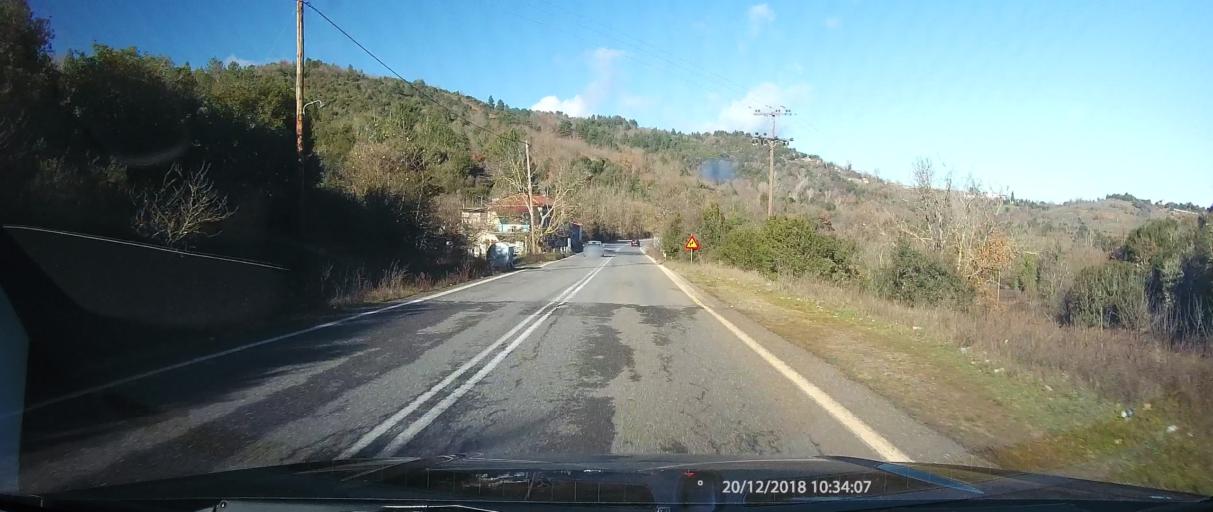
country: GR
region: Peloponnese
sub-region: Nomos Lakonias
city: Kariai
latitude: 37.3465
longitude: 22.4141
